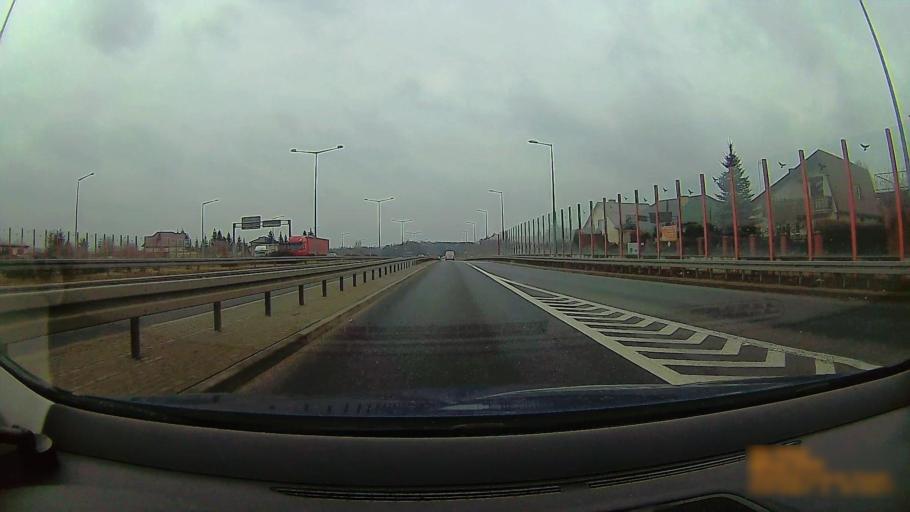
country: PL
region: Greater Poland Voivodeship
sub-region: Powiat koninski
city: Stare Miasto
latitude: 52.1819
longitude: 18.2238
